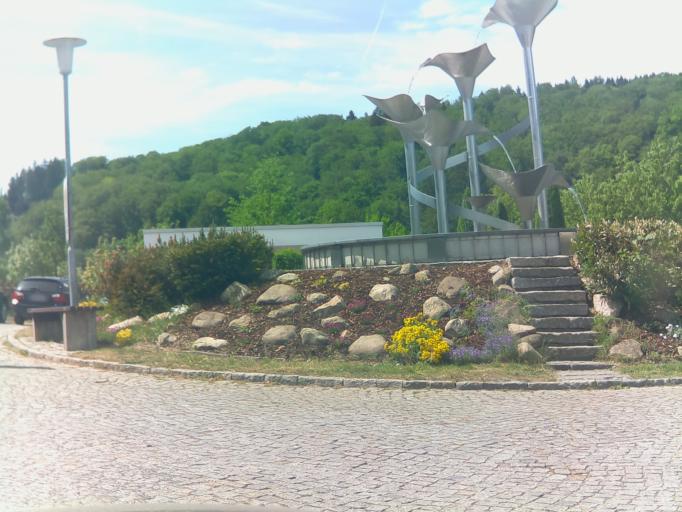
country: DE
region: Saxony-Anhalt
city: Huttenrode
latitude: 51.7409
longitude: 10.9184
